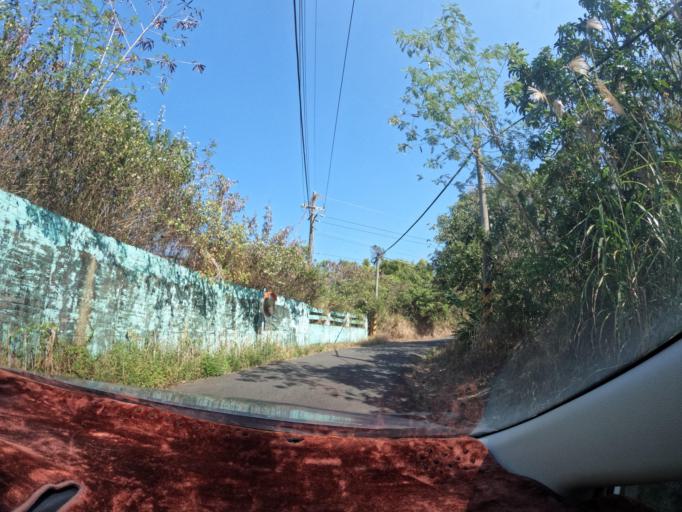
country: TW
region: Taiwan
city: Yujing
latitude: 23.0483
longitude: 120.3687
